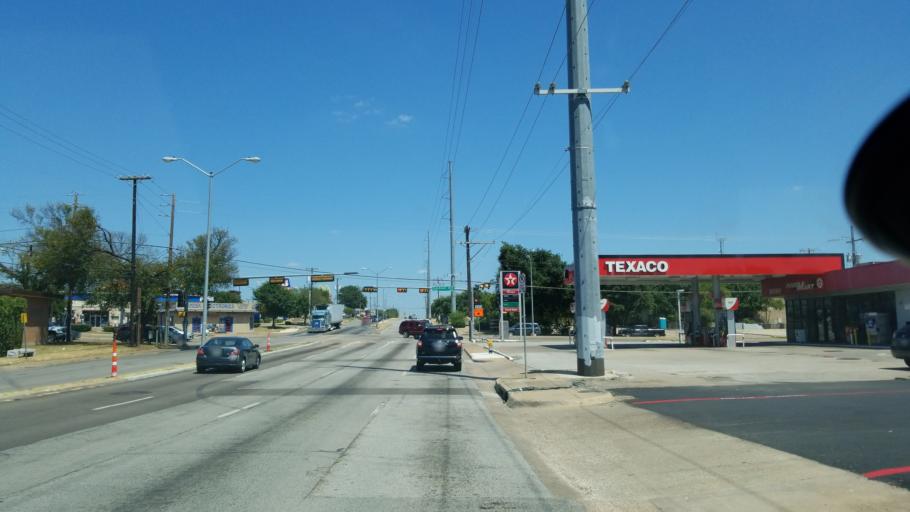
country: US
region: Texas
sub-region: Dallas County
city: Cockrell Hill
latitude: 32.7204
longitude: -96.8923
